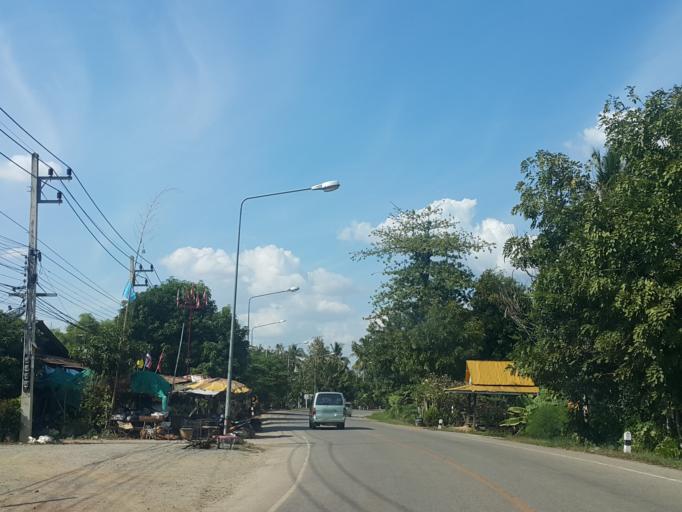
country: TH
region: Sukhothai
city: Sawankhalok
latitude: 17.2951
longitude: 99.8277
